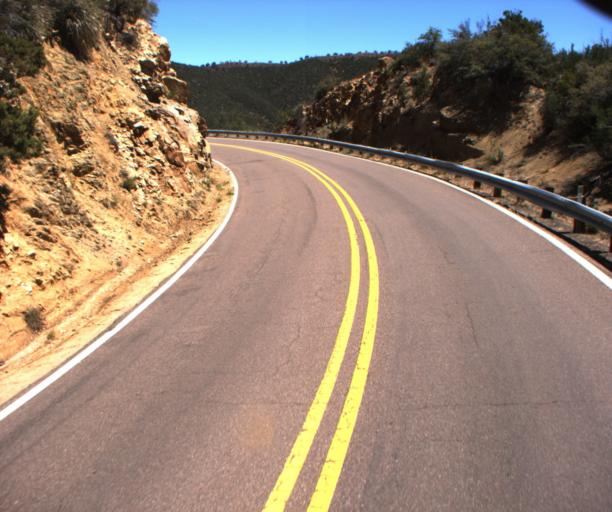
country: US
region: Arizona
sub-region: Yavapai County
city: Prescott
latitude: 34.4590
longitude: -112.5178
